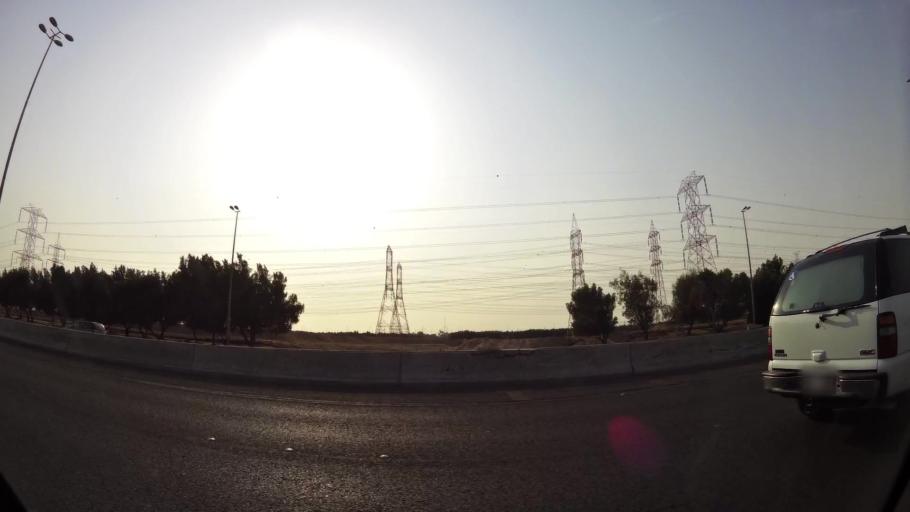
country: KW
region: Mubarak al Kabir
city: Sabah as Salim
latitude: 29.2561
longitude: 48.0451
